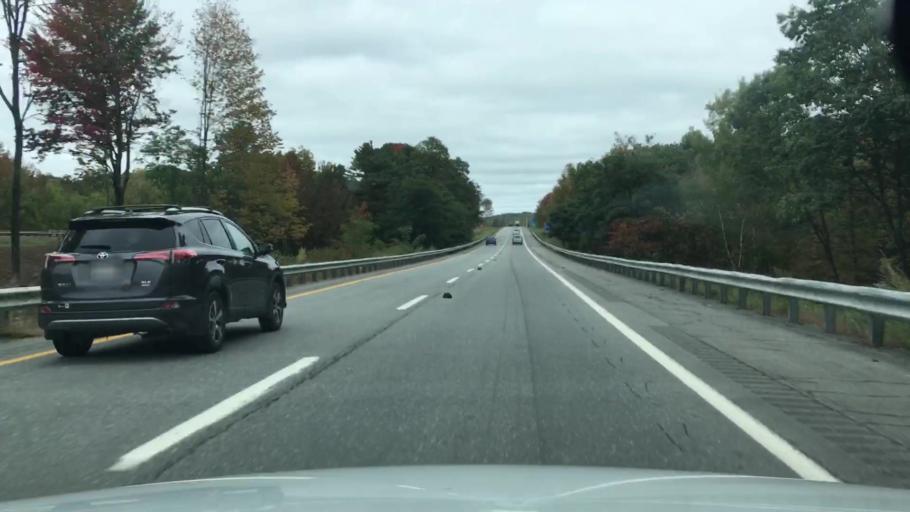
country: US
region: Maine
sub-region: Somerset County
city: Fairfield
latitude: 44.5835
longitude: -69.6243
